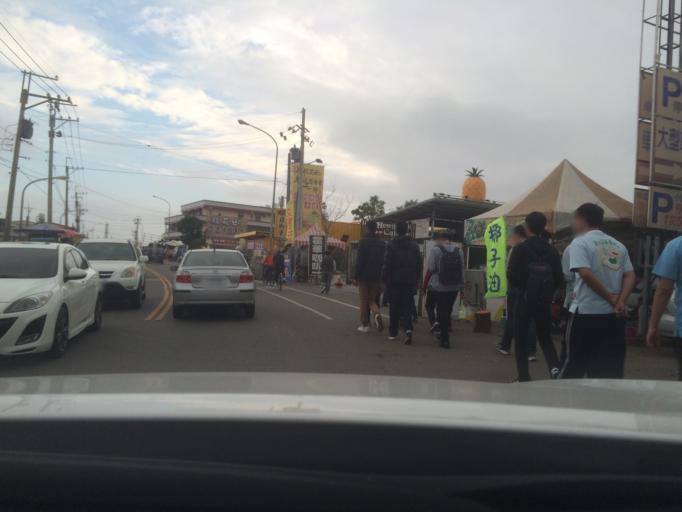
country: TW
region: Taiwan
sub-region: Nantou
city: Nantou
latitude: 23.9336
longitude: 120.6378
